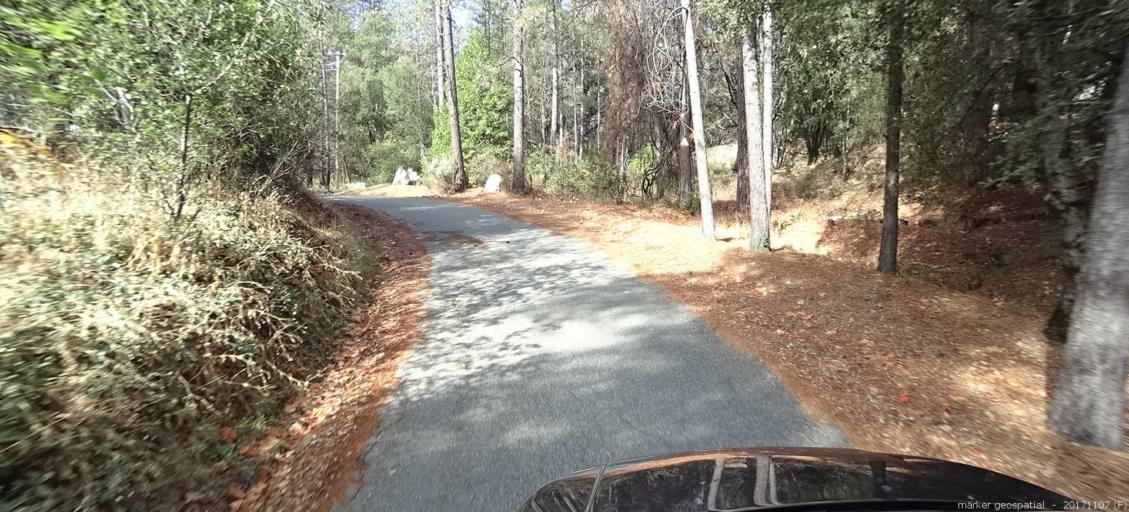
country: US
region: California
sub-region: Shasta County
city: Shasta
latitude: 40.5450
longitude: -122.5789
